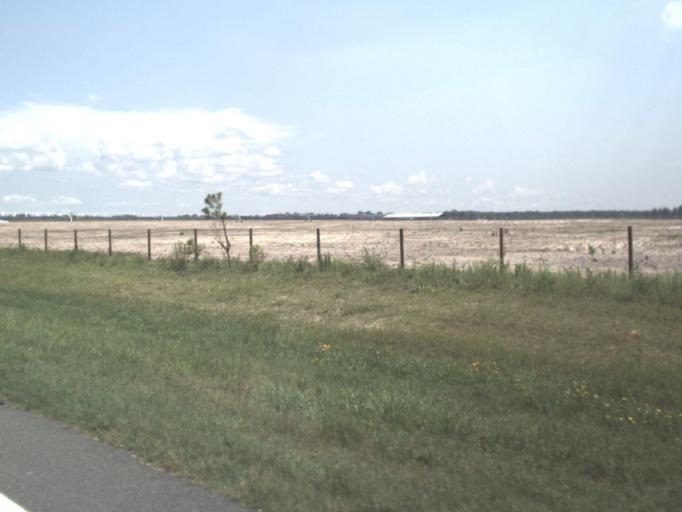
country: US
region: Florida
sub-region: Lafayette County
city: Mayo
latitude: 30.0851
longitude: -83.2221
